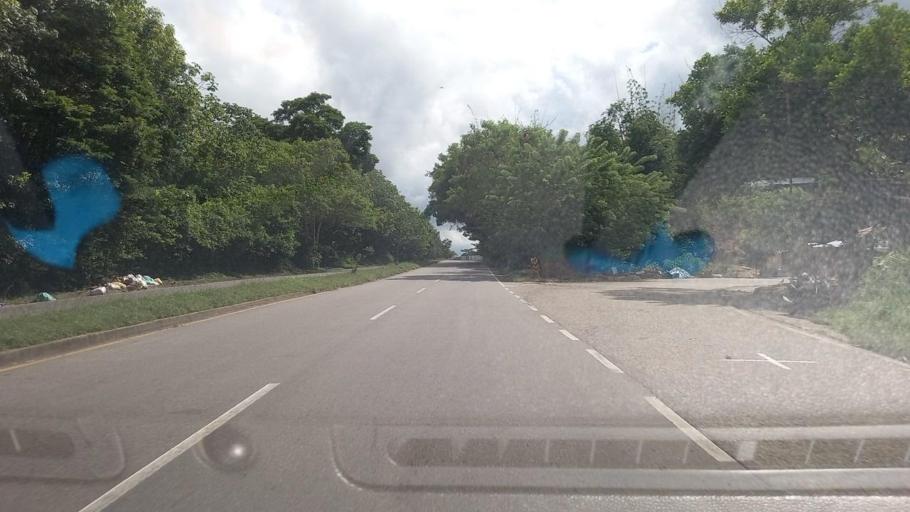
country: CO
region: Santander
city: Barrancabermeja
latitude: 7.1191
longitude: -73.6141
